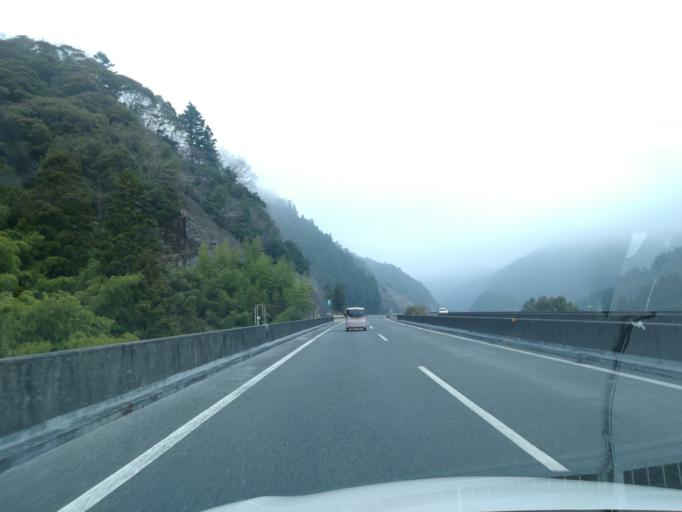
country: JP
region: Ehime
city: Kawanoecho
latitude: 33.7811
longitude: 133.6612
